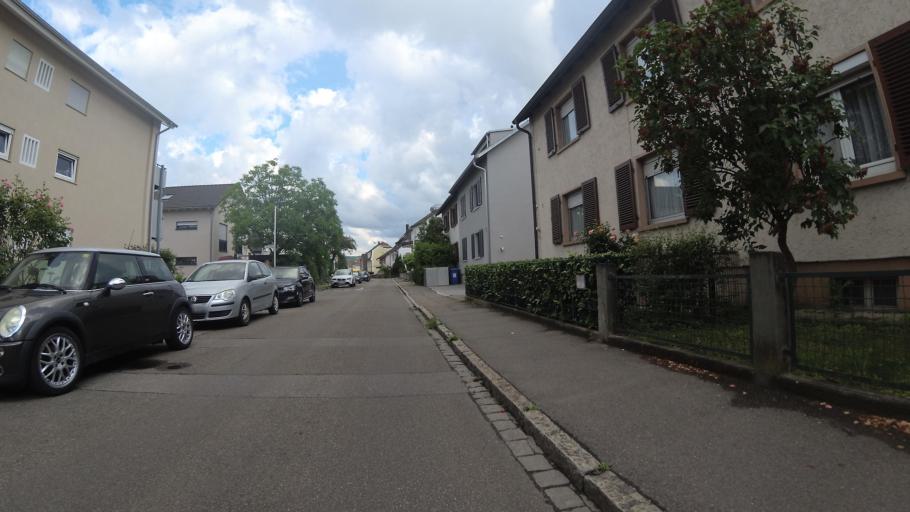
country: DE
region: Baden-Wuerttemberg
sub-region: Freiburg Region
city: Weil am Rhein
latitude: 47.5931
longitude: 7.6263
